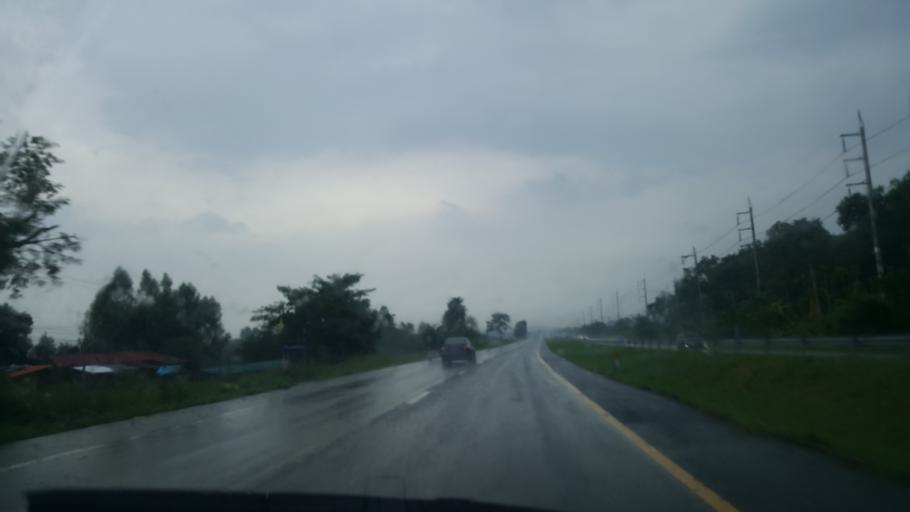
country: TH
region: Chon Buri
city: Ban Talat Bueng
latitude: 12.9810
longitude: 101.0597
